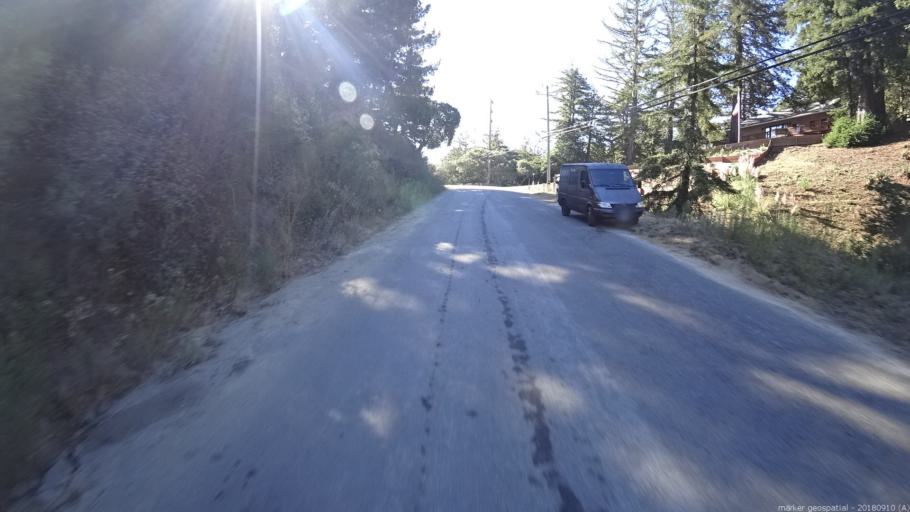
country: US
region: California
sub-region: Monterey County
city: Carmel Valley Village
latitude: 36.3868
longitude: -121.8713
